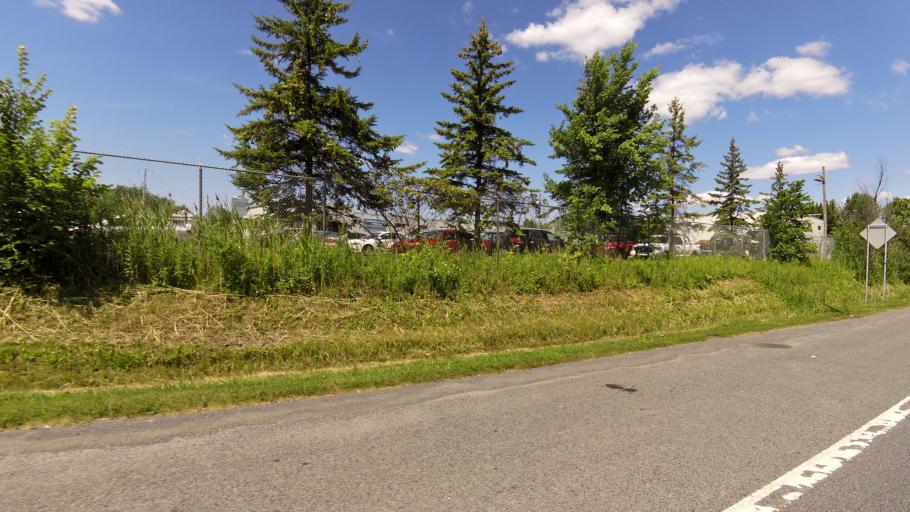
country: CA
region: Quebec
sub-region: Monteregie
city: Richelieu
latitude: 45.4409
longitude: -73.2458
